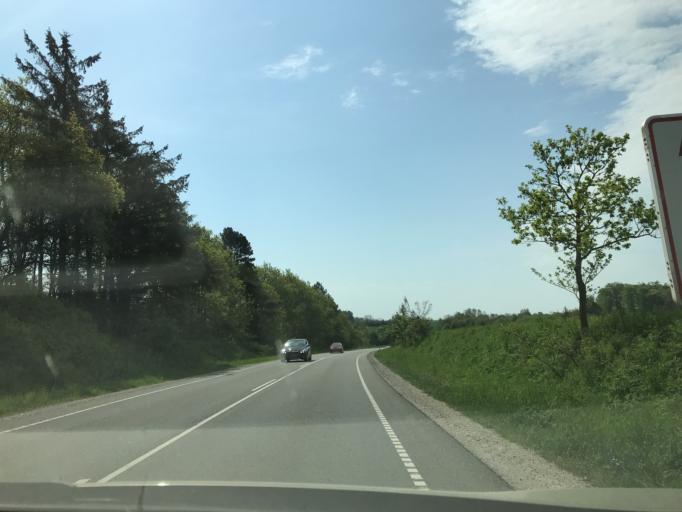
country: DK
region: South Denmark
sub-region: Middelfart Kommune
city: Ejby
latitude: 55.3871
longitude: 9.9167
